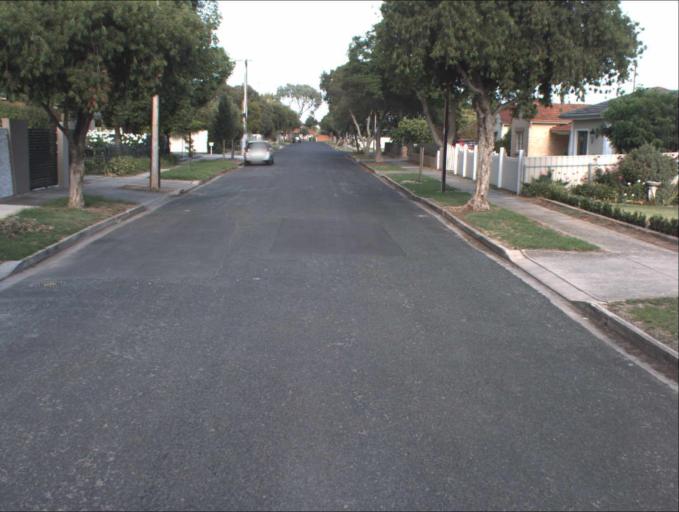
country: AU
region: South Australia
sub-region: Port Adelaide Enfield
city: Klemzig
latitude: -34.8728
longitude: 138.6228
